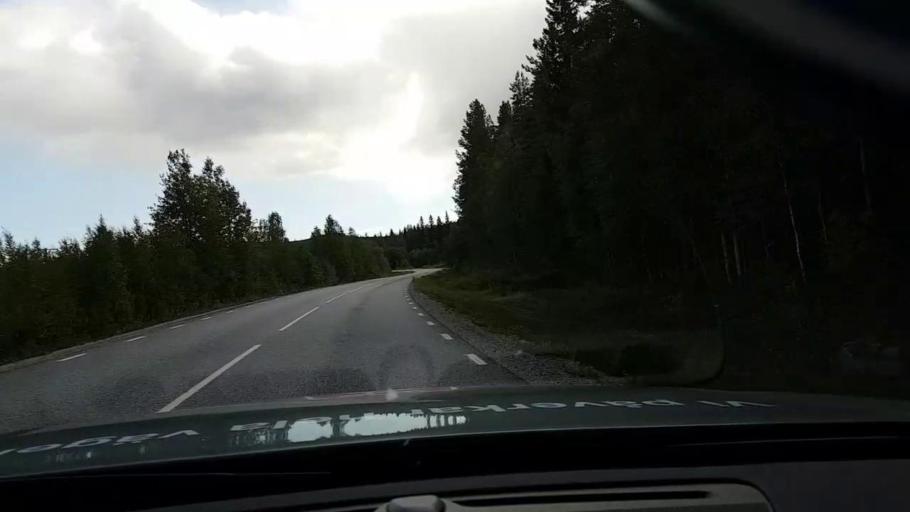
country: SE
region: Vaesternorrland
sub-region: OErnskoeldsviks Kommun
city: Bredbyn
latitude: 63.6897
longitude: 17.7706
